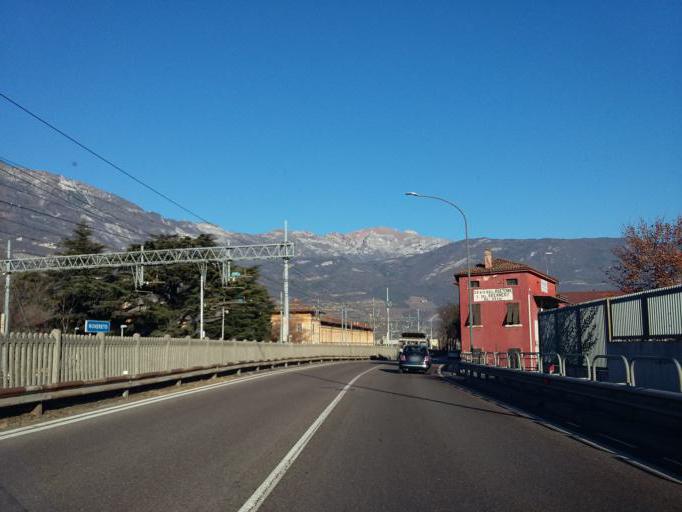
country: IT
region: Trentino-Alto Adige
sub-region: Provincia di Trento
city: Rovereto
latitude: 45.8936
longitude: 11.0343
